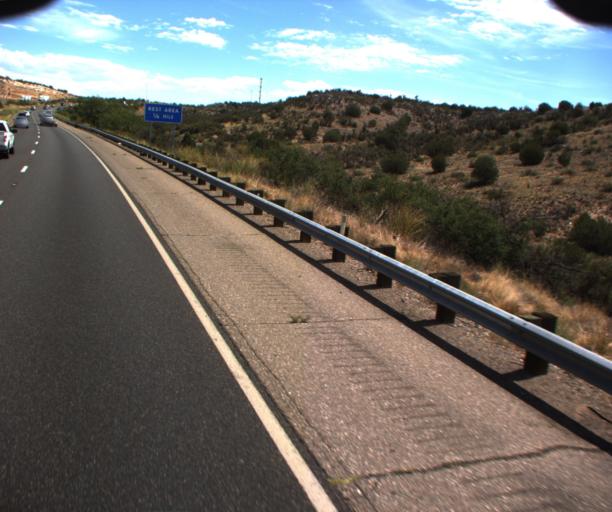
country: US
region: Arizona
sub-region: Yavapai County
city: Lake Montezuma
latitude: 34.6680
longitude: -111.7806
